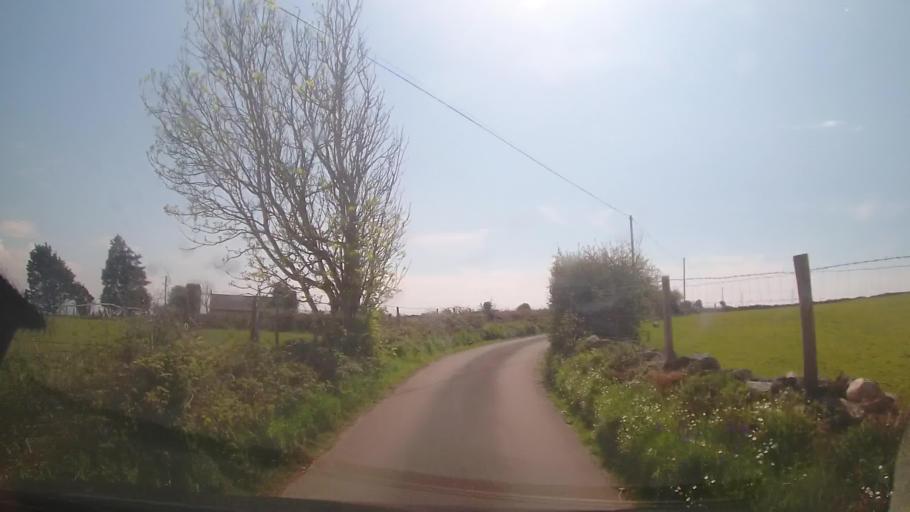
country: GB
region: Wales
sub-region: Gwynedd
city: Porthmadog
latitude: 52.9189
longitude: -4.1812
